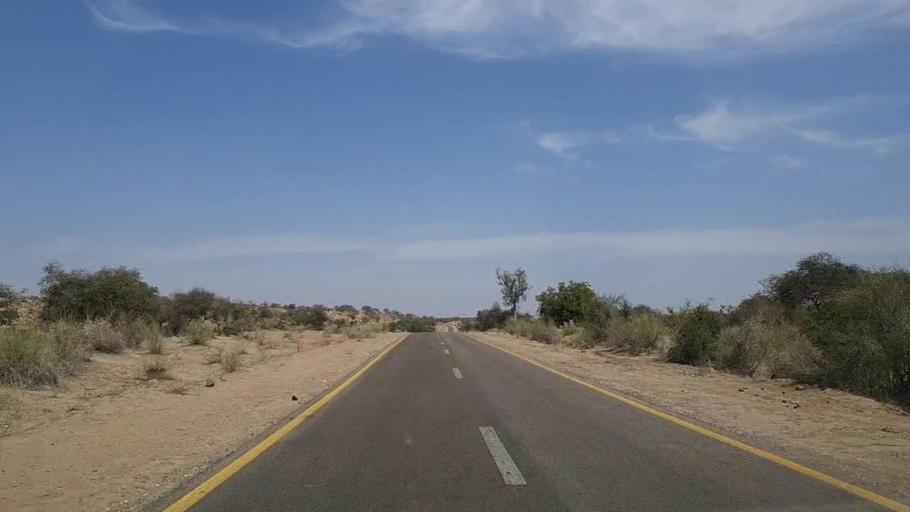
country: PK
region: Sindh
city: Mithi
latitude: 24.8269
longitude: 69.8270
